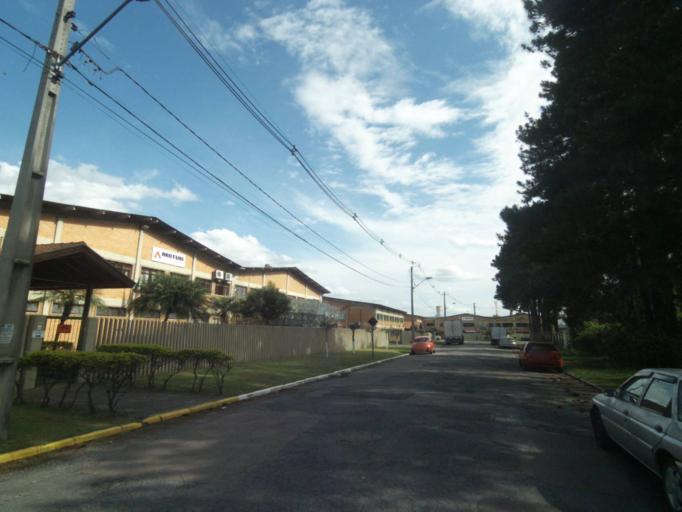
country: BR
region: Parana
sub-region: Curitiba
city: Curitiba
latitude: -25.4990
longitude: -49.3294
